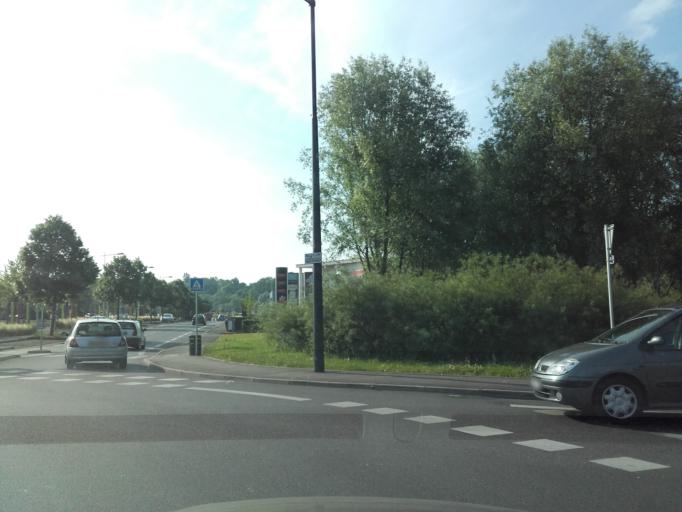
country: FR
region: Centre
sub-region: Departement d'Indre-et-Loire
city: Joue-les-Tours
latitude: 47.3652
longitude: 0.6751
